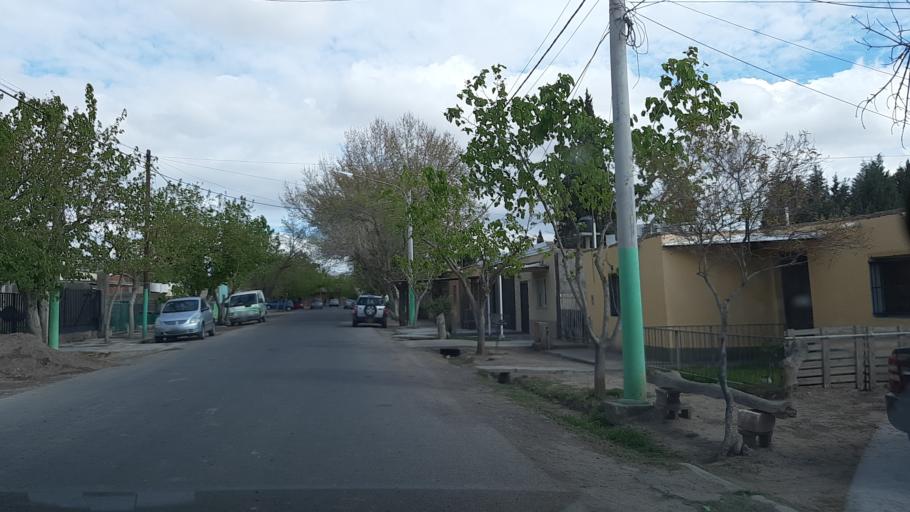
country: AR
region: San Juan
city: San Juan
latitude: -31.5368
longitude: -68.5771
